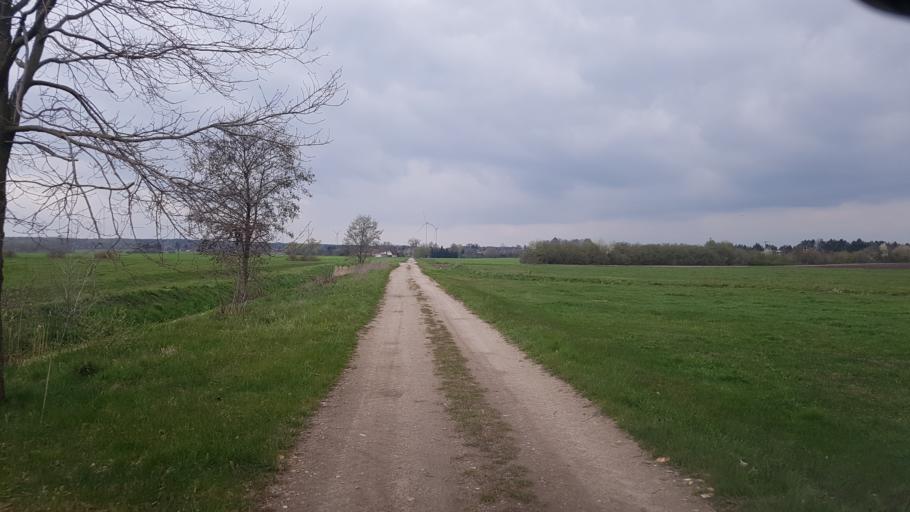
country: DE
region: Brandenburg
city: Sallgast
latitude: 51.6365
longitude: 13.8709
